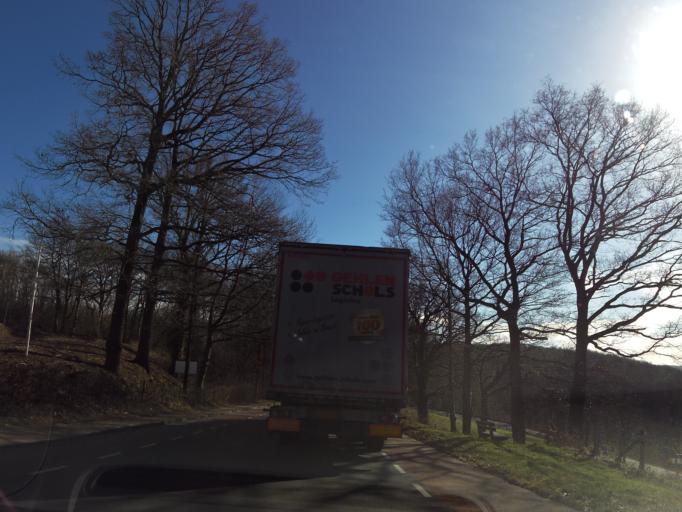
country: BE
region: Flanders
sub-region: Provincie Limburg
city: Sint-Pieters-Voeren
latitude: 50.7725
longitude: 5.8737
